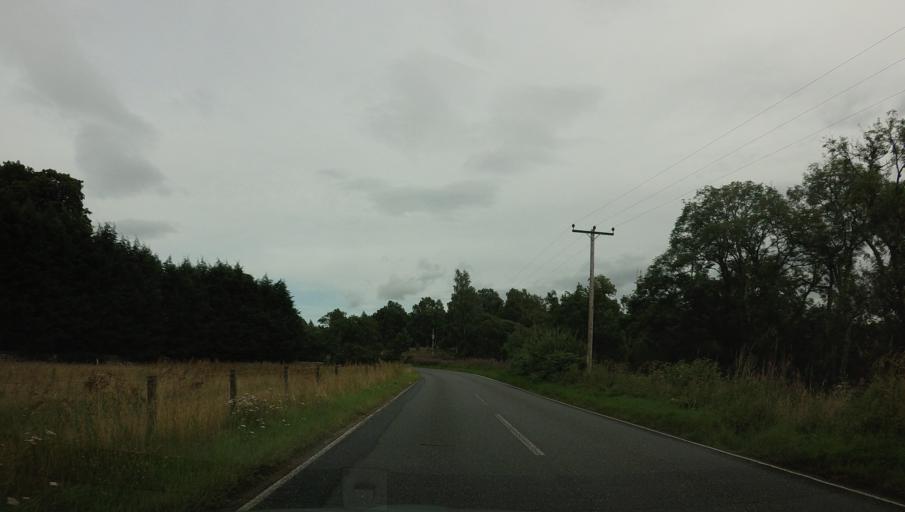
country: GB
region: Scotland
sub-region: Aberdeenshire
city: Banchory
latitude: 57.0590
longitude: -2.5503
